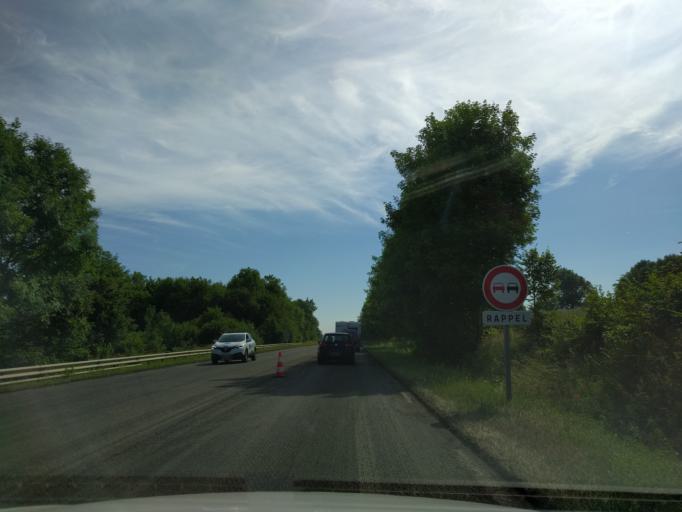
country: FR
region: Picardie
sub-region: Departement de l'Oise
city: Breteuil
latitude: 49.5792
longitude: 2.2414
